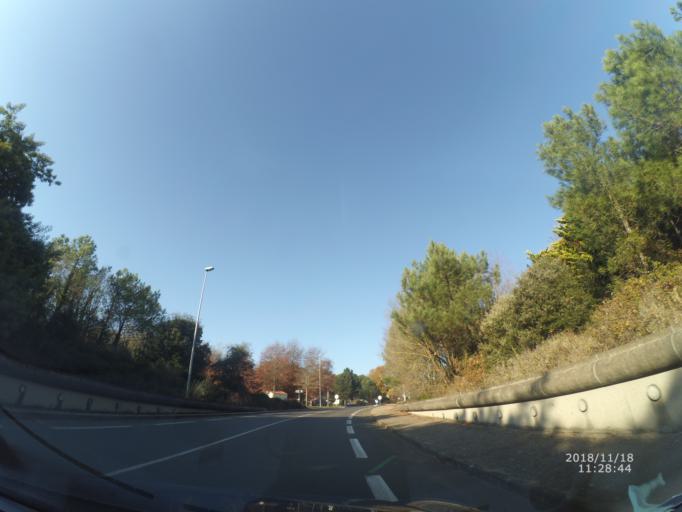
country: FR
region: Pays de la Loire
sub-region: Departement de la Loire-Atlantique
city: Saint-Michel-Chef-Chef
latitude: 47.2146
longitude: -2.1518
